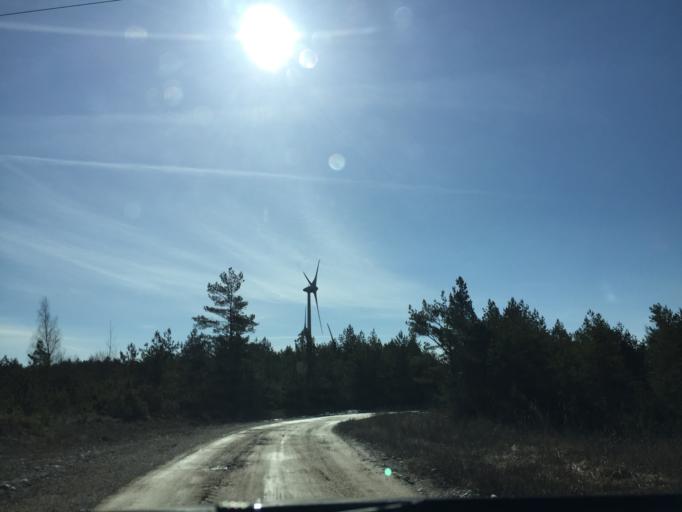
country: EE
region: Laeaene
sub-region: Haapsalu linn
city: Haapsalu
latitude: 58.6344
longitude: 23.5245
